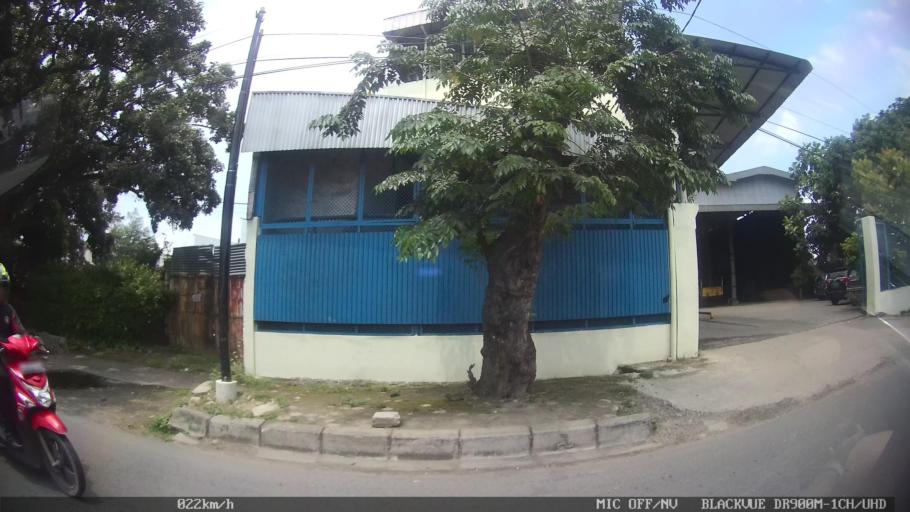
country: ID
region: North Sumatra
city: Medan
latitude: 3.6369
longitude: 98.6667
